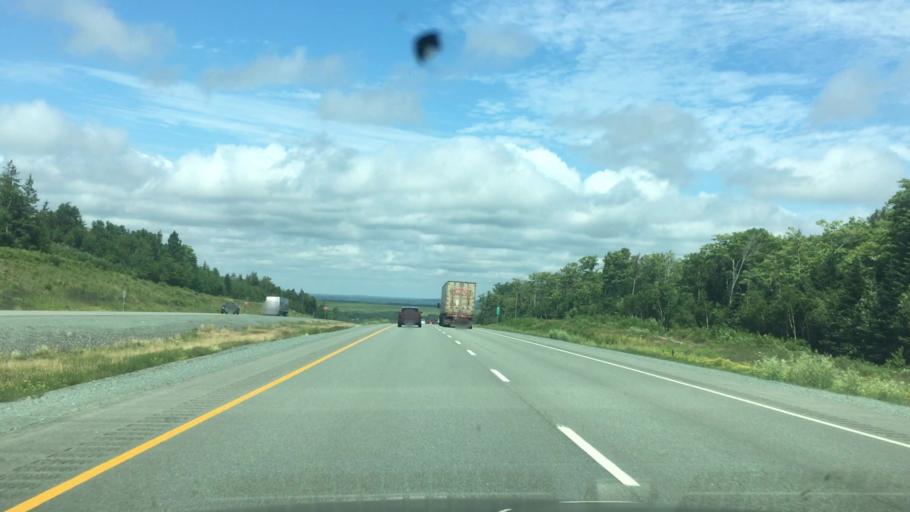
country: CA
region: Nova Scotia
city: Oxford
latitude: 45.5923
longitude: -63.7249
